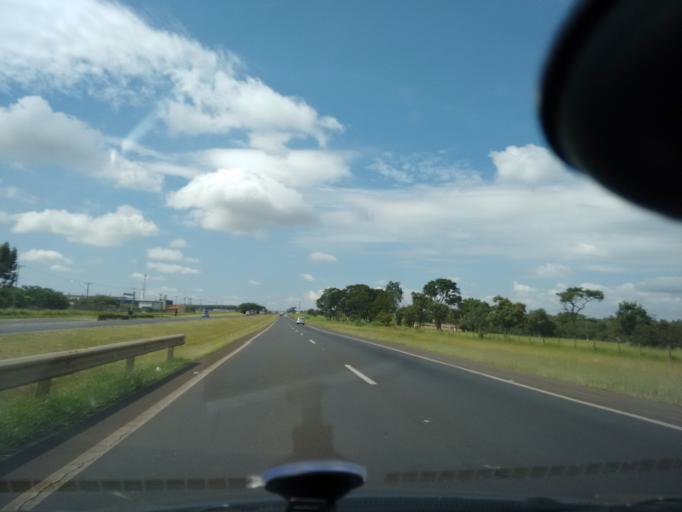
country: BR
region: Sao Paulo
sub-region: Ibate
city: Ibate
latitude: -21.9363
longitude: -48.0128
